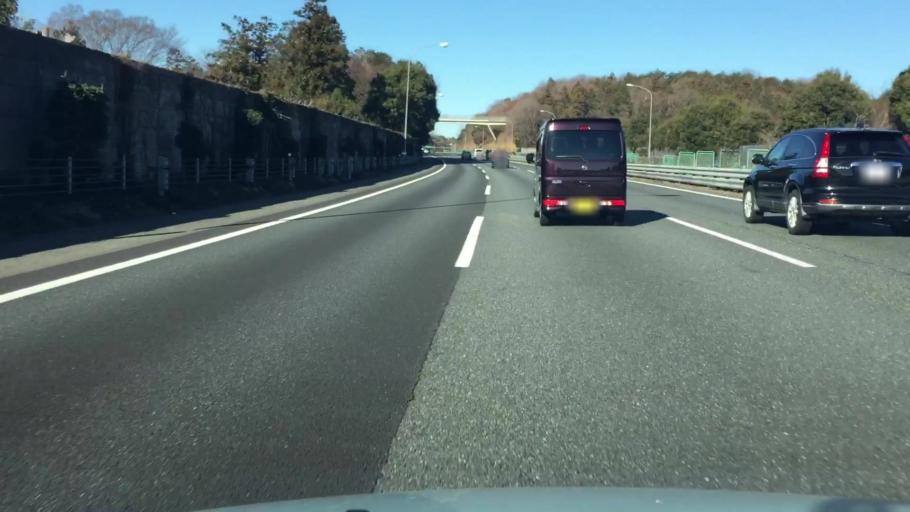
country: JP
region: Saitama
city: Ogawa
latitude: 36.0538
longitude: 139.3390
